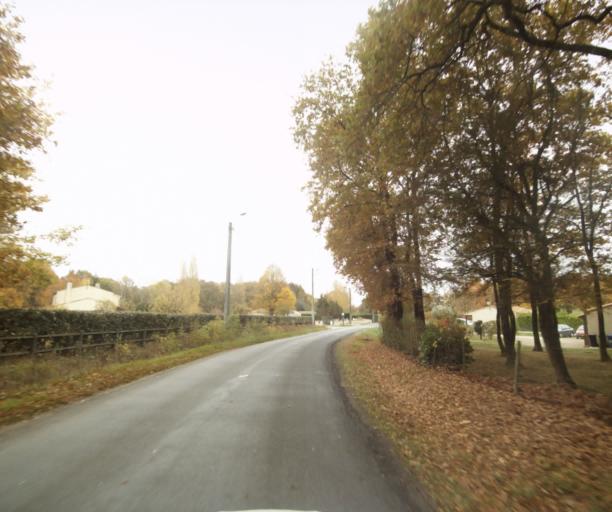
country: FR
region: Poitou-Charentes
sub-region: Departement de la Charente-Maritime
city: Chermignac
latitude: 45.7171
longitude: -0.6939
